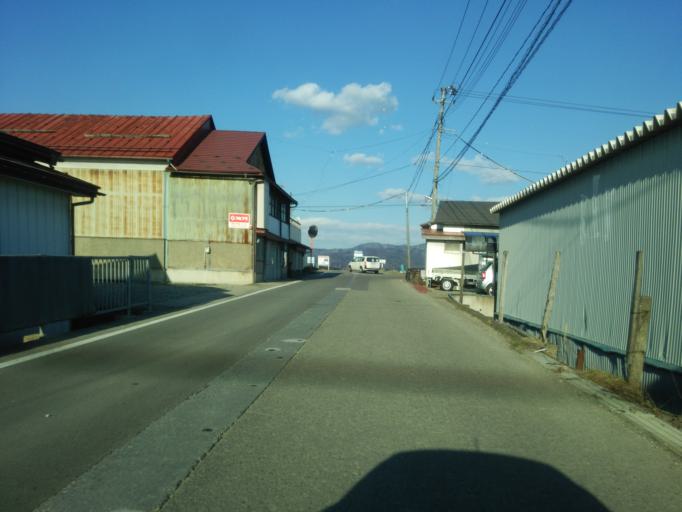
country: JP
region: Fukushima
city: Kitakata
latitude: 37.4745
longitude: 139.8953
